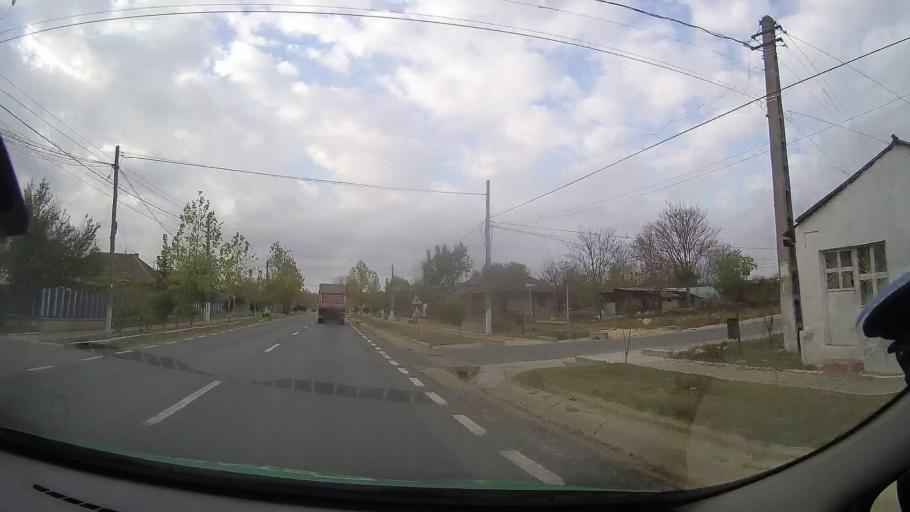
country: RO
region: Constanta
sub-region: Comuna Mircea Voda
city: Satu Nou
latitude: 44.2669
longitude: 28.2283
